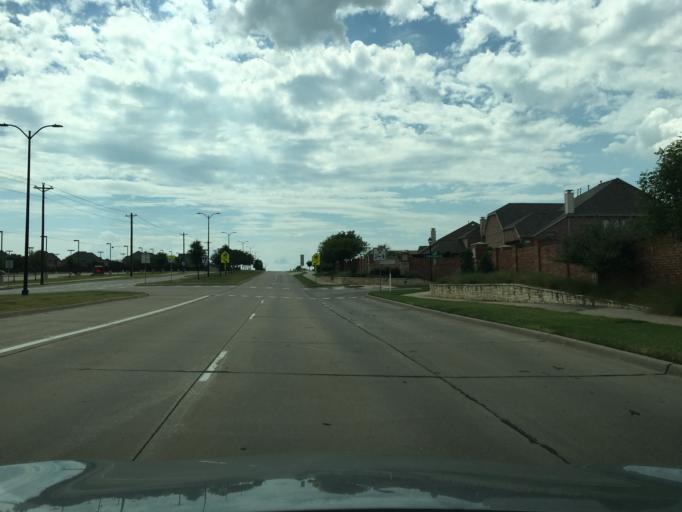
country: US
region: Texas
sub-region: Collin County
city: Frisco
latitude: 33.1331
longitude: -96.8629
